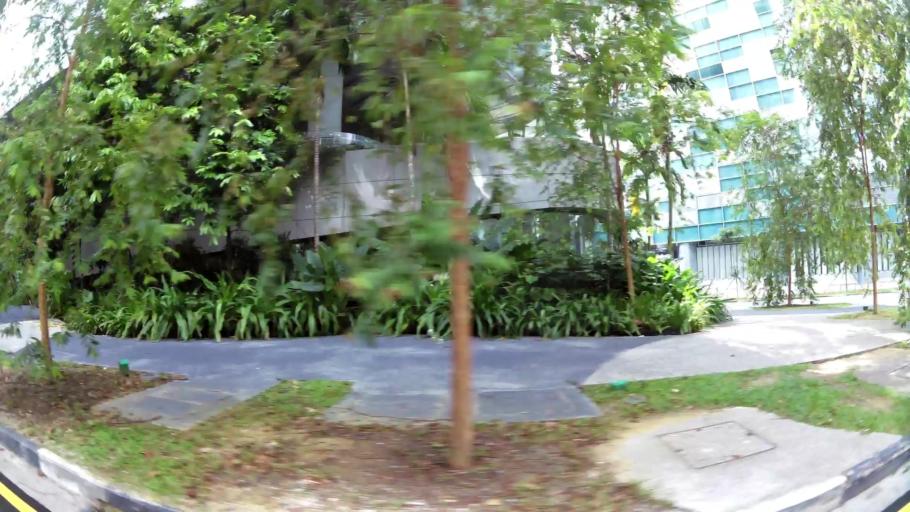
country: SG
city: Singapore
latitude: 1.2996
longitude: 103.7889
